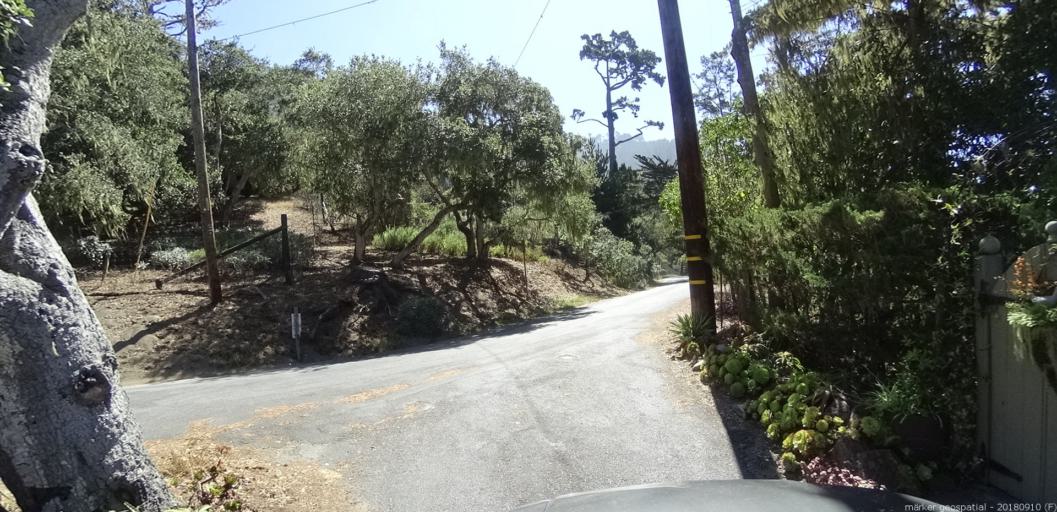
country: US
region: California
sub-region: Monterey County
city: Carmel-by-the-Sea
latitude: 36.5001
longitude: -121.9342
